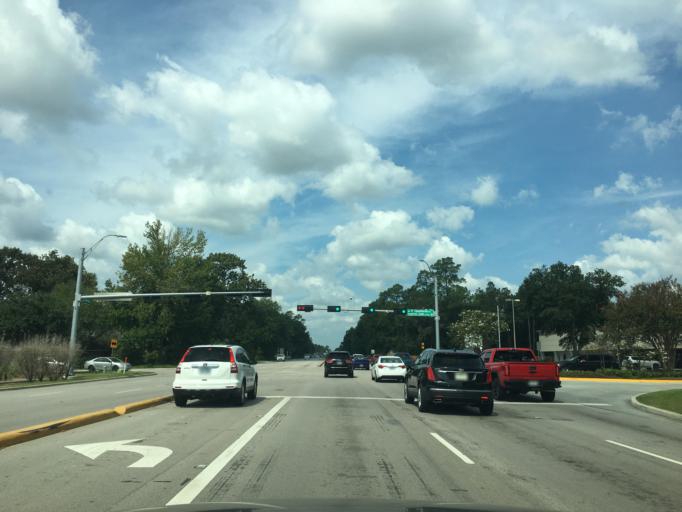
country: US
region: Texas
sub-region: Harris County
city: Spring
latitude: 30.1234
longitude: -95.4100
